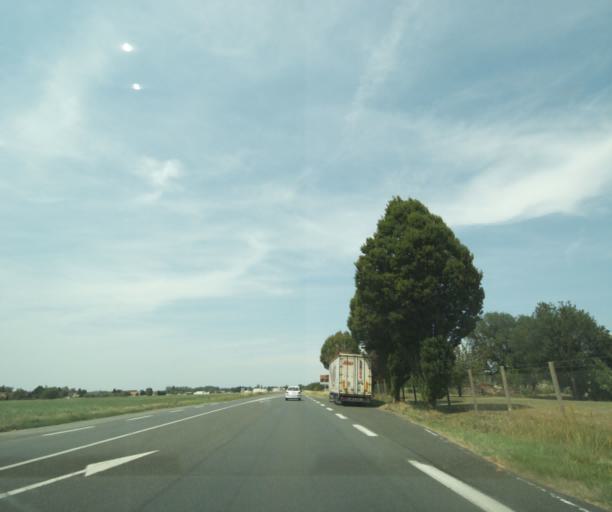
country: FR
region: Poitou-Charentes
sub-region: Departement de la Vienne
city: Dange-Saint-Romain
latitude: 46.9522
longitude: 0.6075
